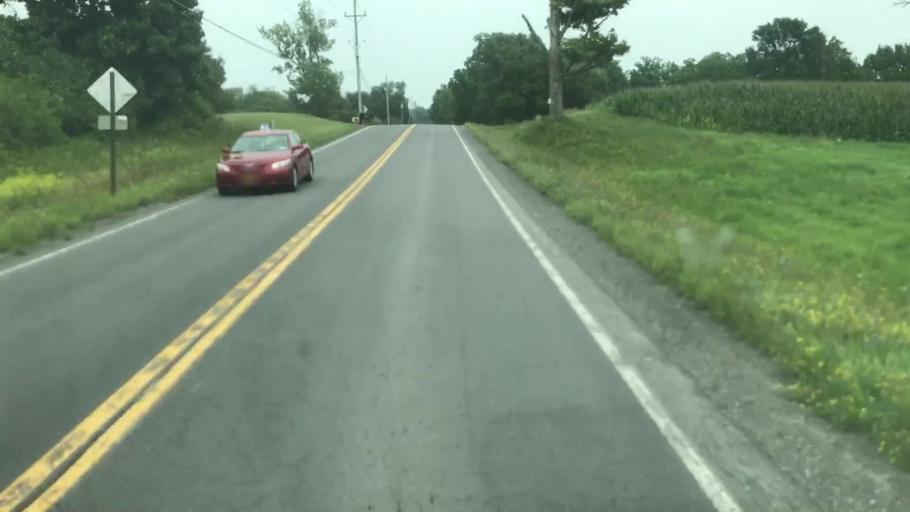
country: US
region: New York
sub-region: Cayuga County
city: Melrose Park
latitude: 42.9539
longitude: -76.5024
